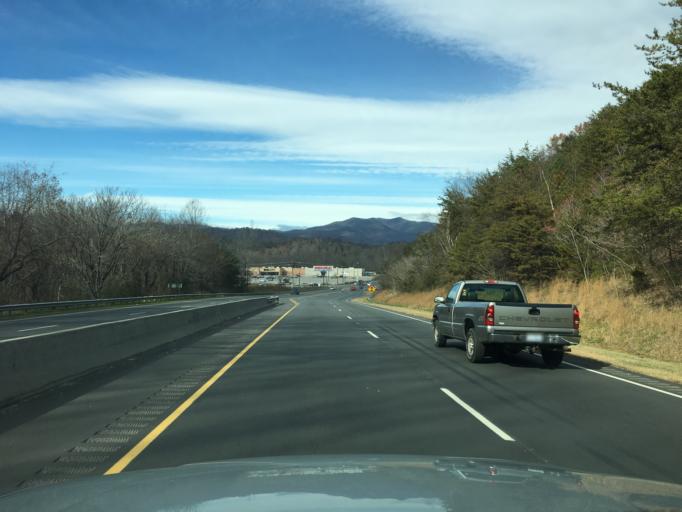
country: US
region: North Carolina
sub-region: McDowell County
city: Marion
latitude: 35.7016
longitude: -82.0340
